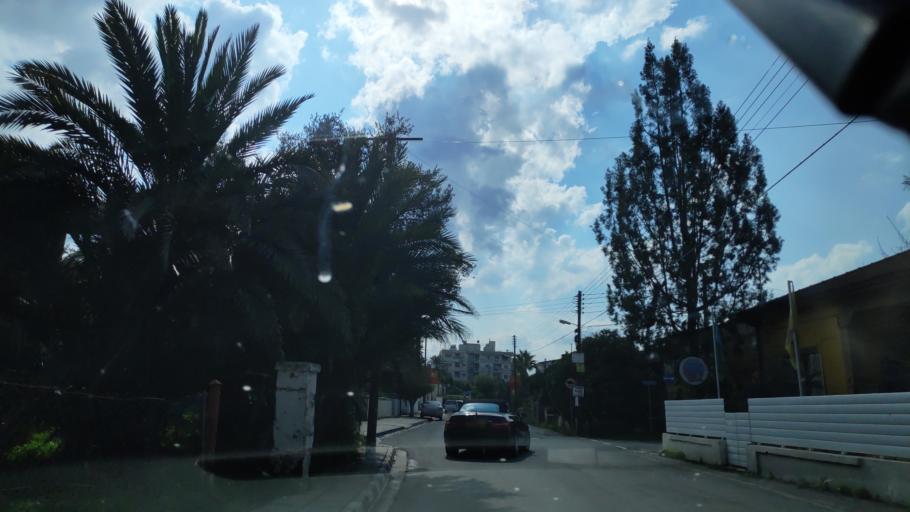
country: CY
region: Lefkosia
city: Nicosia
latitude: 35.1518
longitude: 33.3459
